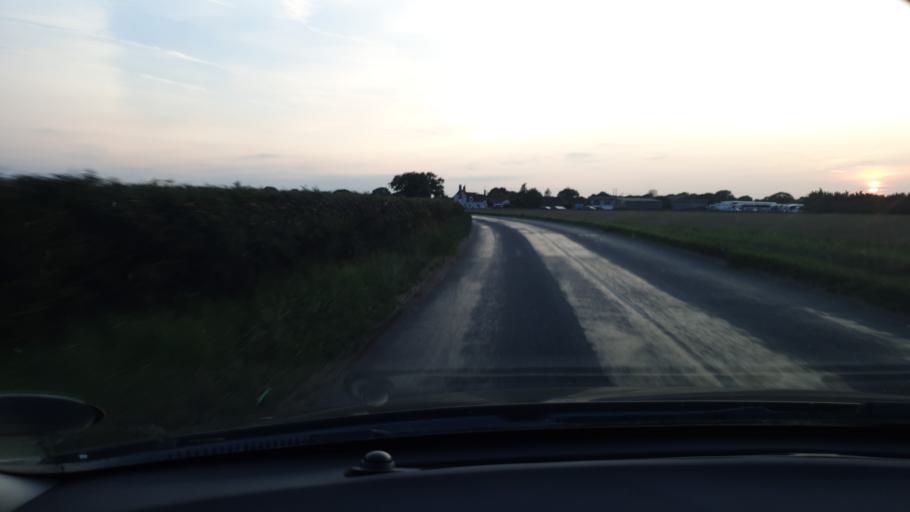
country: GB
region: England
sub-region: Essex
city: Great Bentley
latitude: 51.8530
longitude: 1.0471
